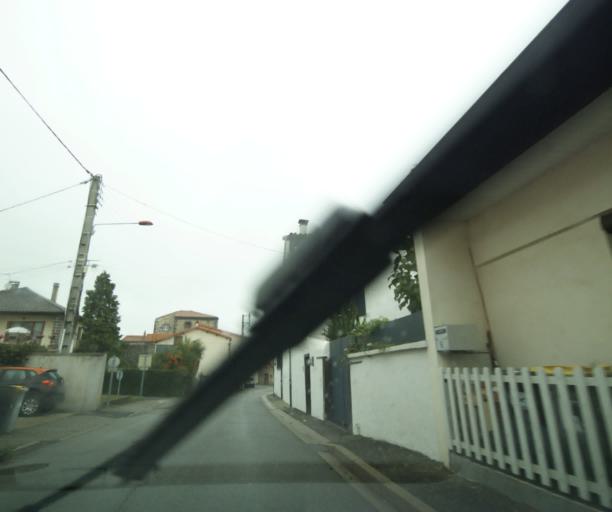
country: FR
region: Auvergne
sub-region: Departement du Puy-de-Dome
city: Chateaugay
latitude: 45.8507
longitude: 3.0854
